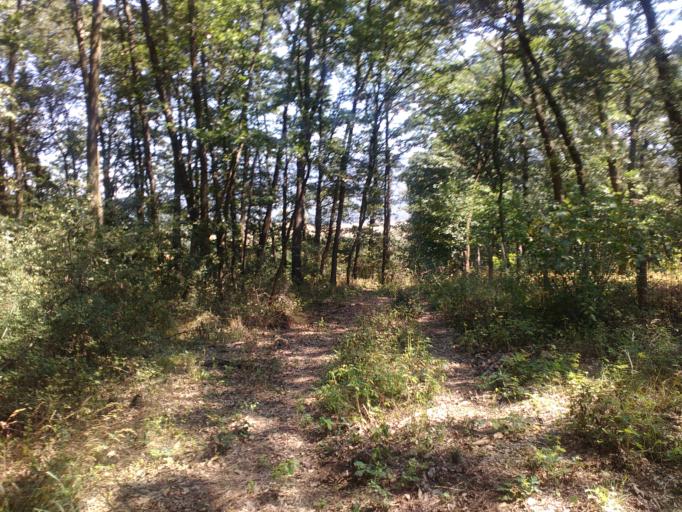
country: HU
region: Komarom-Esztergom
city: Piliscsev
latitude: 47.6683
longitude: 18.8236
